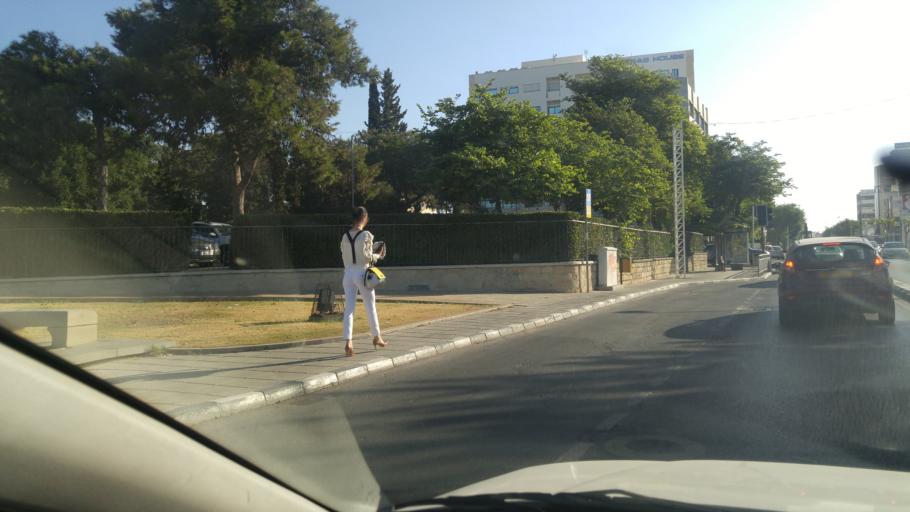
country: CY
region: Limassol
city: Limassol
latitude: 34.6870
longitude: 33.0388
